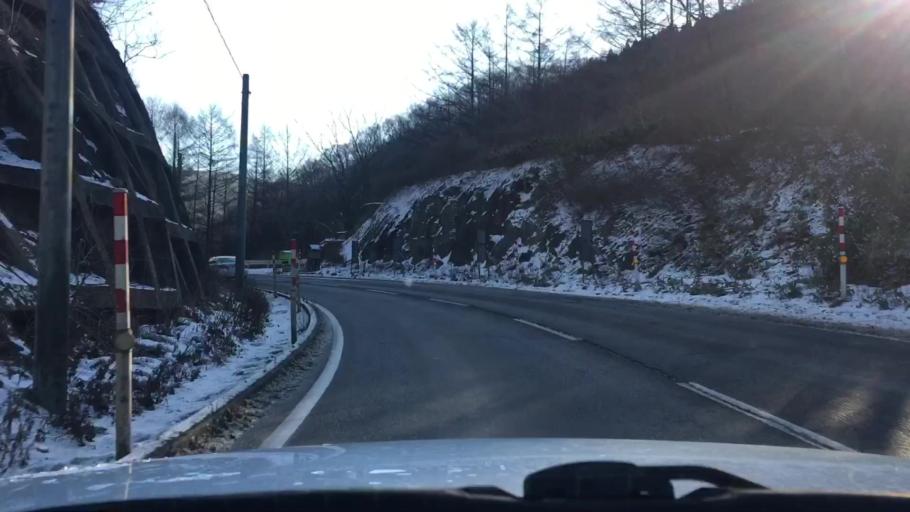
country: JP
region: Iwate
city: Morioka-shi
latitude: 39.6656
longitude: 141.3051
